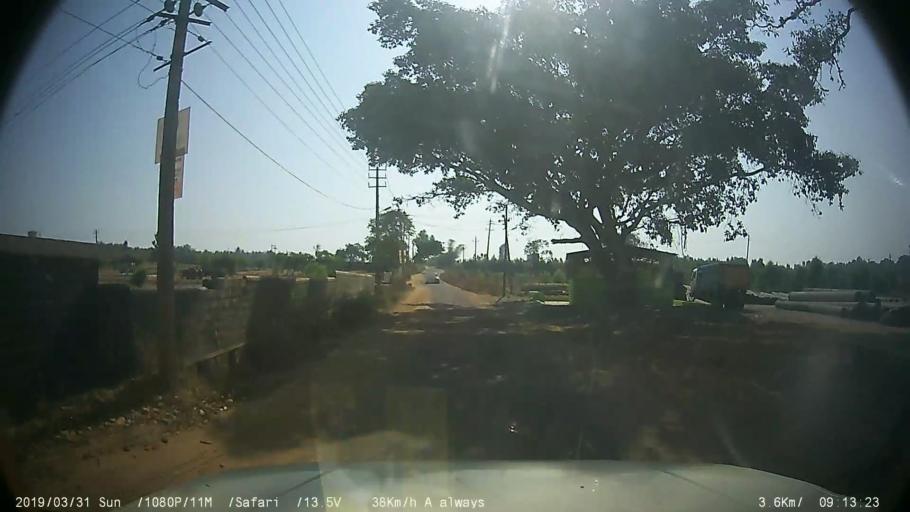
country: IN
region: Karnataka
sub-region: Bangalore Urban
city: Anekal
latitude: 12.8138
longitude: 77.6448
